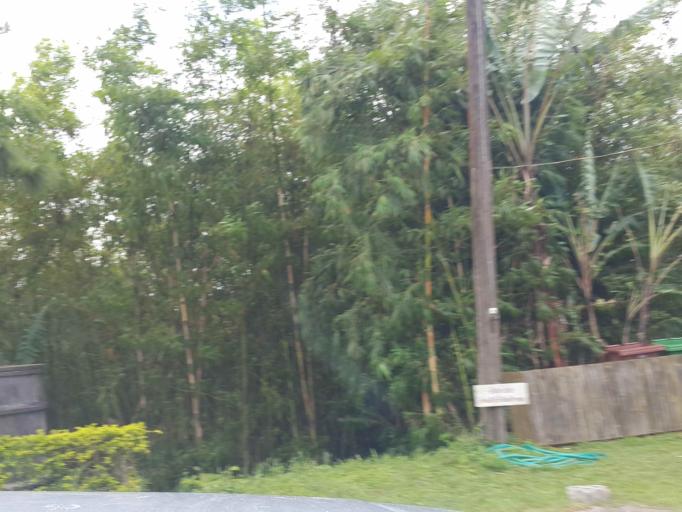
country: TH
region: Tak
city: Tak
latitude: 16.7809
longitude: 98.9299
